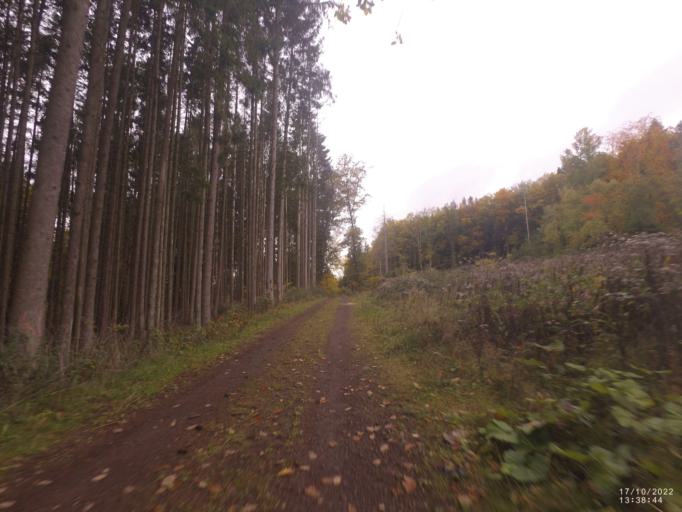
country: DE
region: Rheinland-Pfalz
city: Horscheid
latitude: 50.2206
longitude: 6.8689
